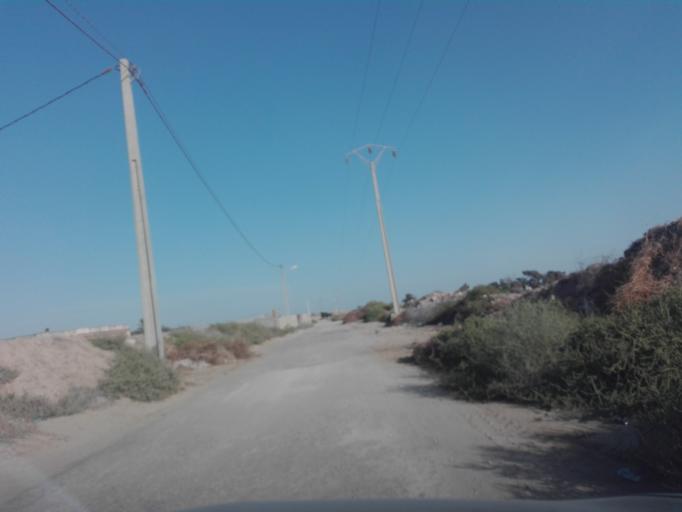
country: TN
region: Qabis
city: Gabes
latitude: 33.9583
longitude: 10.0627
